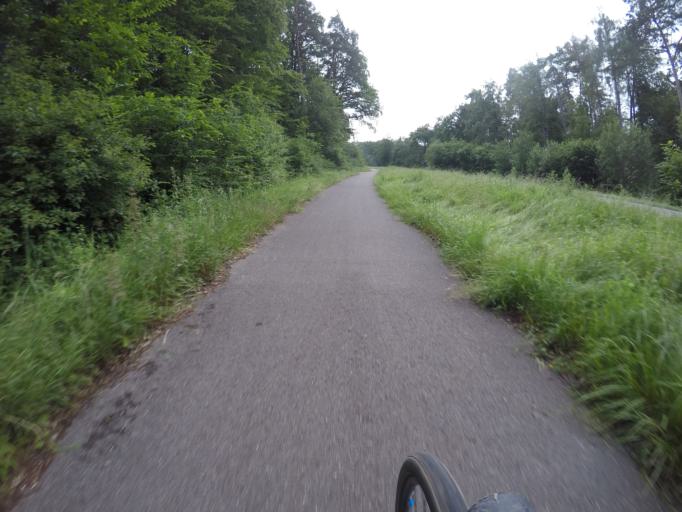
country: DE
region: Baden-Wuerttemberg
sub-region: Regierungsbezirk Stuttgart
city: Kohlberg
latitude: 48.5691
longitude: 9.3287
